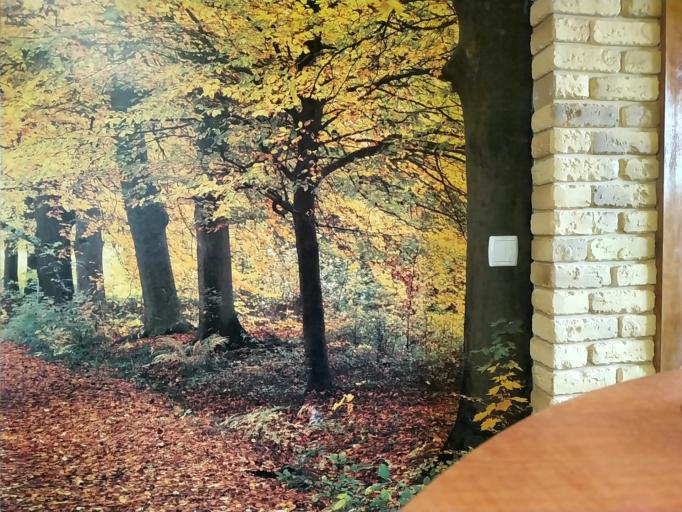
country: RU
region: Novgorod
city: Opechenskiy Posad
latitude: 58.2721
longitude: 34.0012
